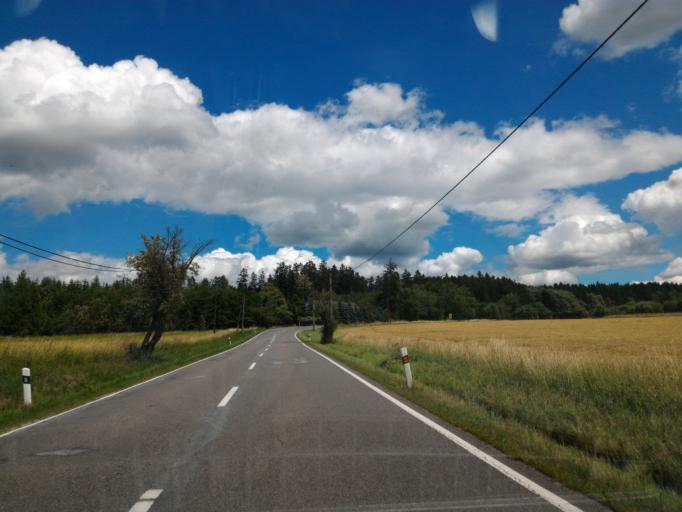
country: CZ
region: Vysocina
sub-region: Okres Jihlava
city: Polna
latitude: 49.4491
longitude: 15.7785
